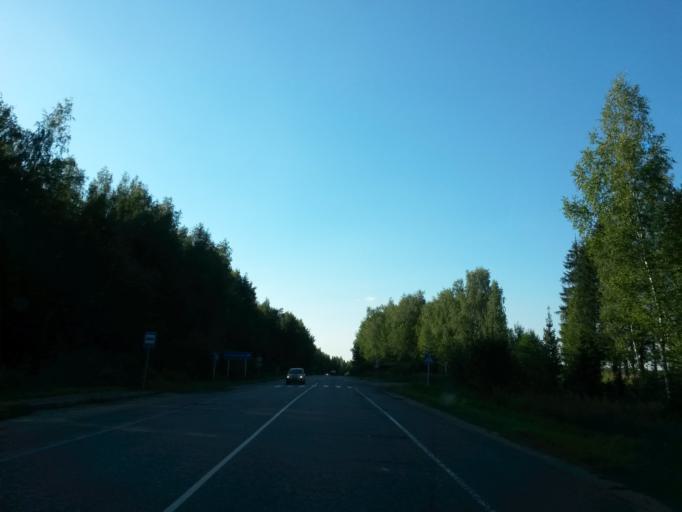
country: RU
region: Ivanovo
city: Pistsovo
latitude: 57.0886
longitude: 40.6678
